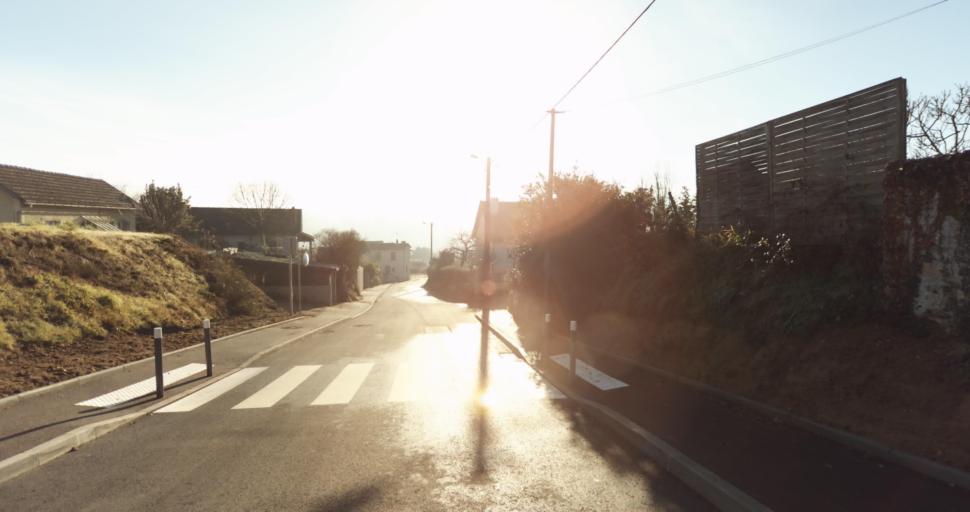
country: FR
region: Limousin
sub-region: Departement de la Haute-Vienne
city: Aixe-sur-Vienne
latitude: 45.7994
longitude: 1.1472
